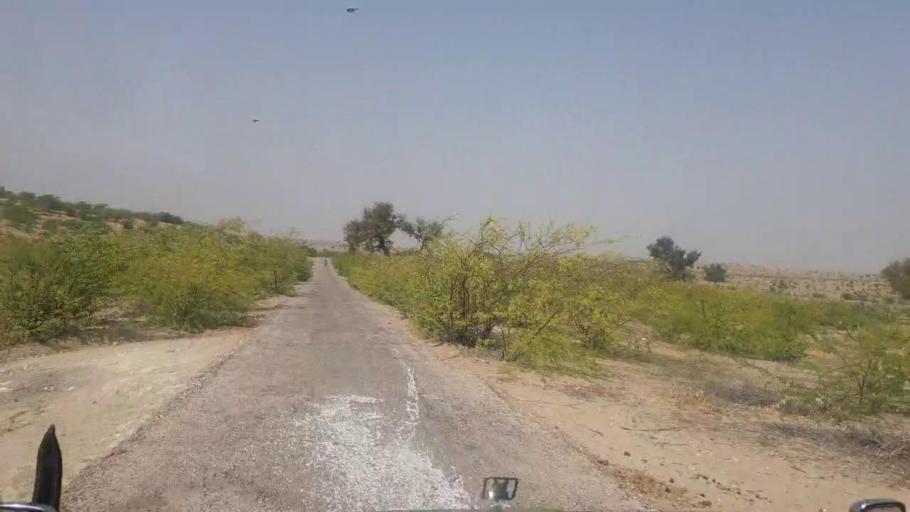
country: PK
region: Sindh
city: Islamkot
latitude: 25.1283
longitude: 70.2205
